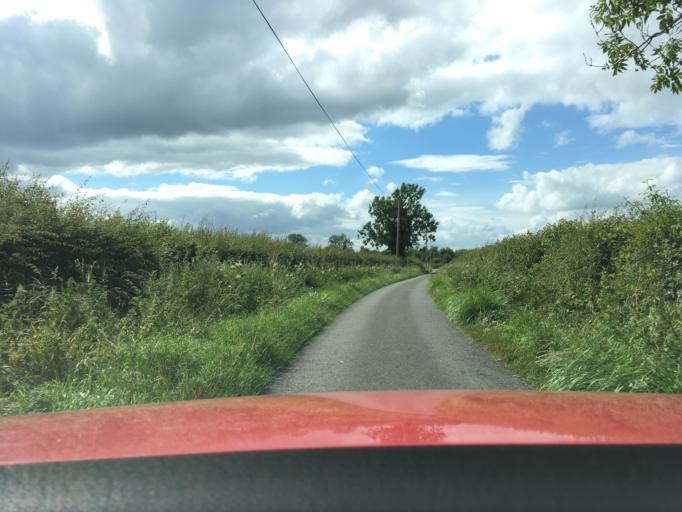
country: GB
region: England
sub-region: Gloucestershire
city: Stonehouse
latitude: 51.8244
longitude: -2.3536
